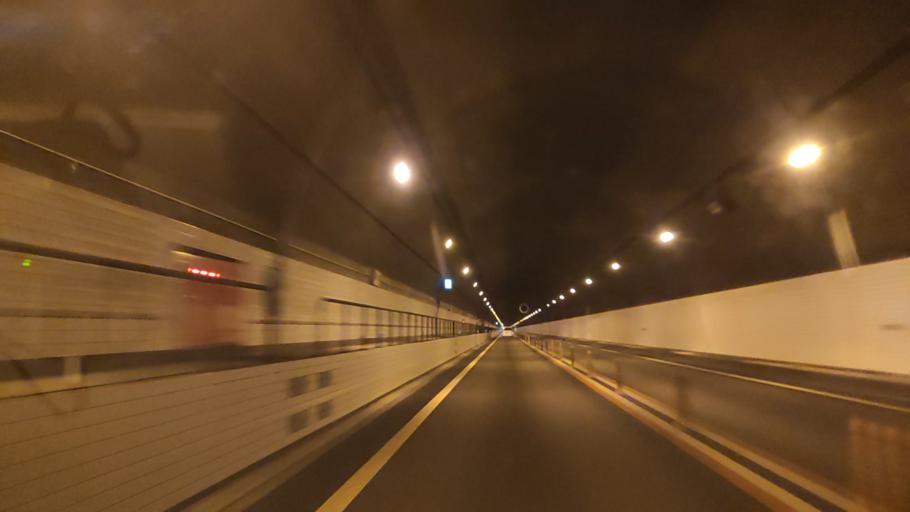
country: JP
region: Ehime
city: Kawanoecho
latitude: 34.0044
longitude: 133.6913
